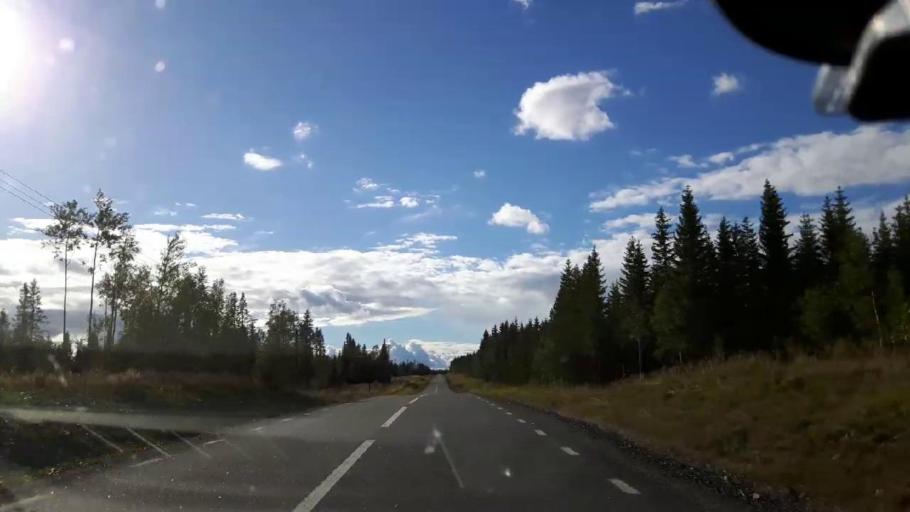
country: SE
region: Jaemtland
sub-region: Stroemsunds Kommun
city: Stroemsund
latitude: 63.5425
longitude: 15.9393
